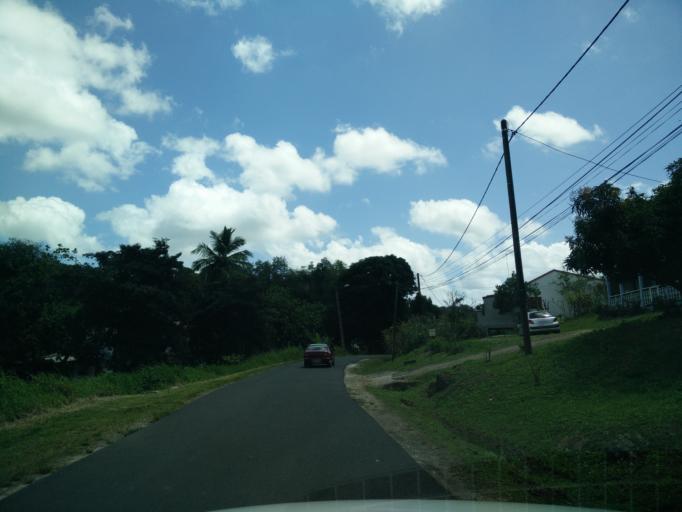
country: GP
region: Guadeloupe
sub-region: Guadeloupe
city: Les Abymes
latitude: 16.2670
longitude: -61.4888
